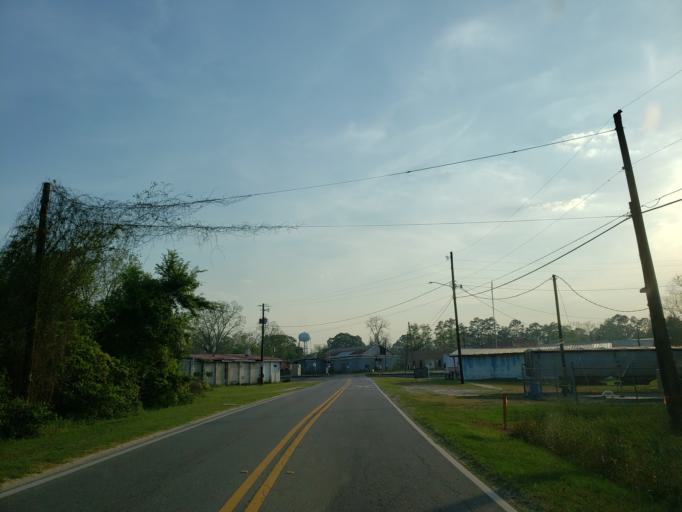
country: US
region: Georgia
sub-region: Cook County
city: Sparks
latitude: 31.1676
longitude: -83.4347
